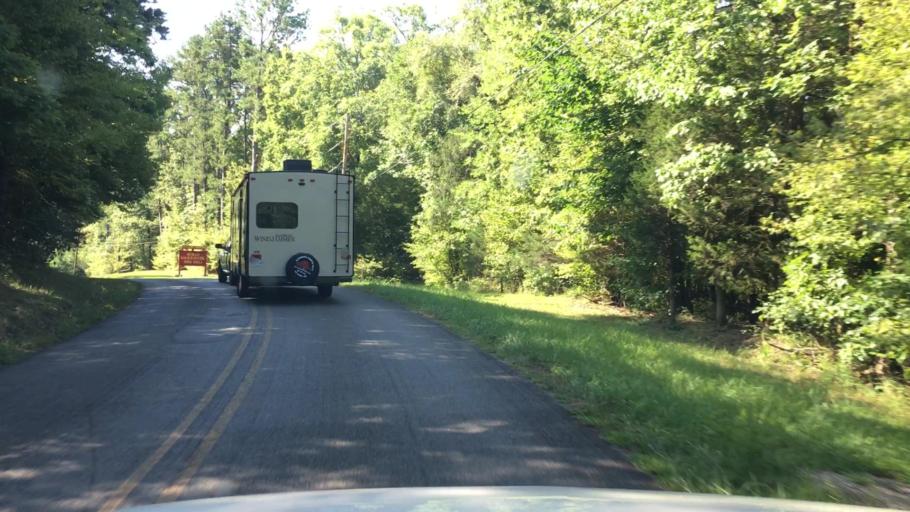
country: US
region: Arkansas
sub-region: Garland County
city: Piney
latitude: 34.5337
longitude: -93.3392
